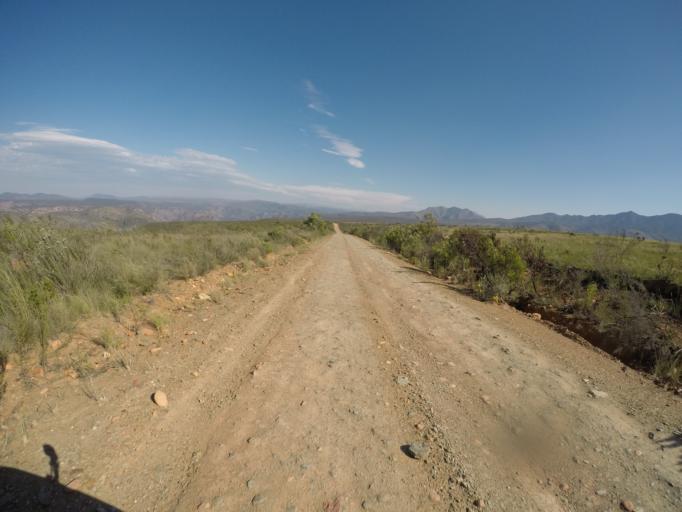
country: ZA
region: Eastern Cape
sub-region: Cacadu District Municipality
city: Kareedouw
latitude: -33.6348
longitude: 24.4730
